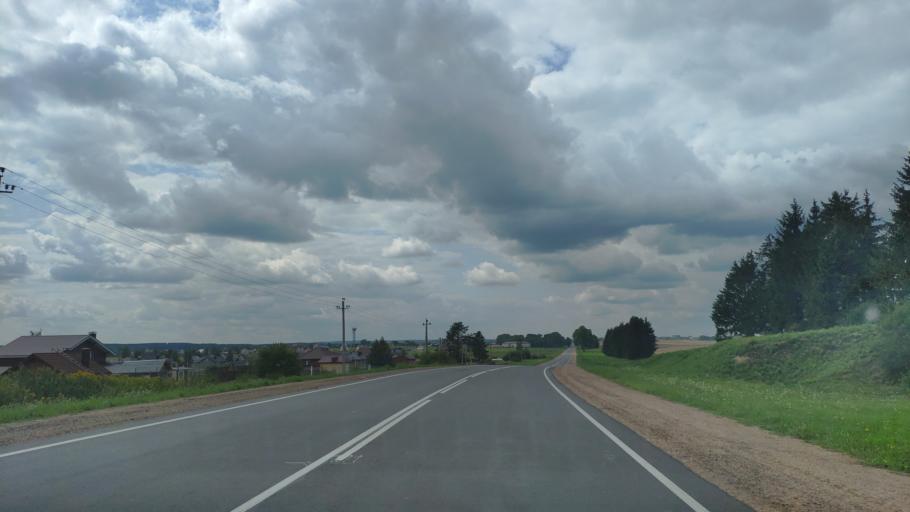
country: BY
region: Minsk
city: Zaslawye
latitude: 54.0050
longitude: 27.3522
